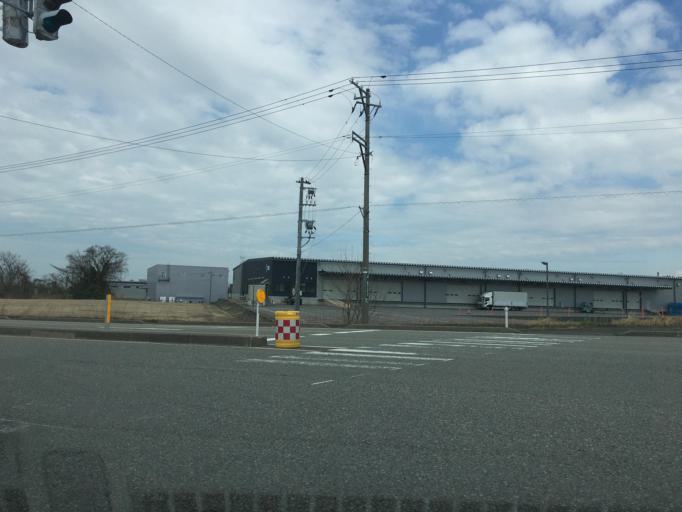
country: JP
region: Toyama
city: Kuragaki-kosugi
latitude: 36.6757
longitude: 137.1292
